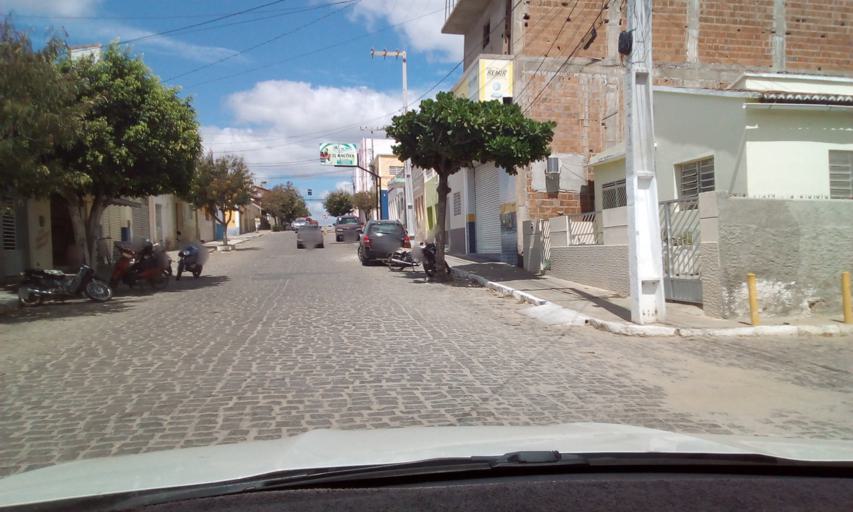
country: BR
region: Paraiba
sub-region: Picui
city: Picui
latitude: -6.5087
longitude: -36.3458
